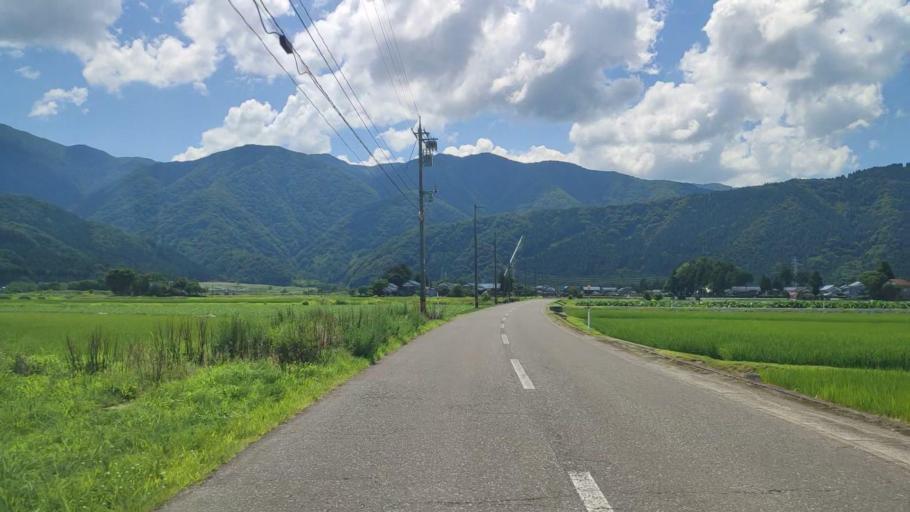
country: JP
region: Fukui
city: Ono
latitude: 35.9467
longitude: 136.5431
